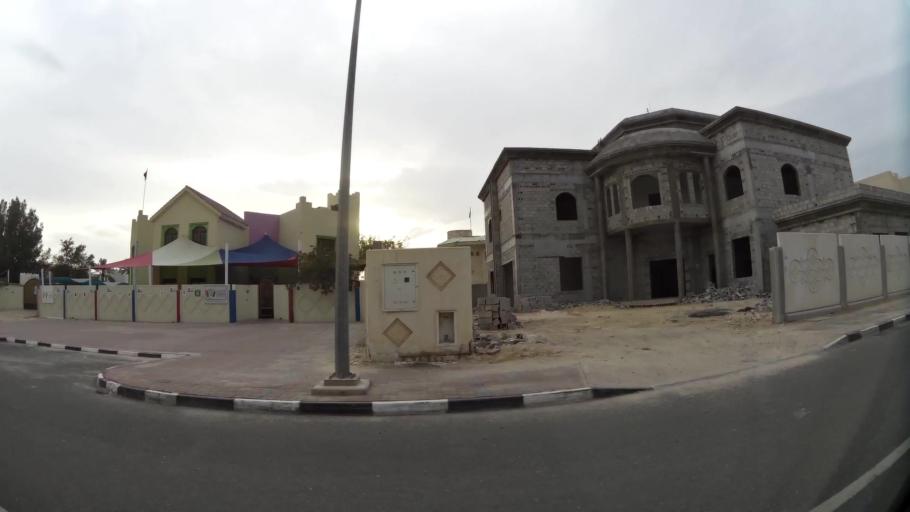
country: QA
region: Baladiyat ad Dawhah
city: Doha
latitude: 25.3243
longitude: 51.5105
